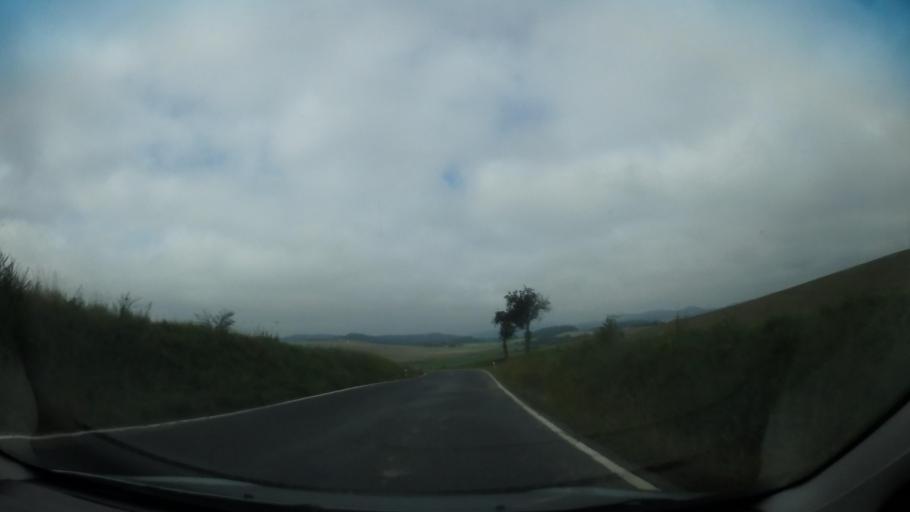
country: CZ
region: Central Bohemia
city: Sedlcany
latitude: 49.7066
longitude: 14.4510
